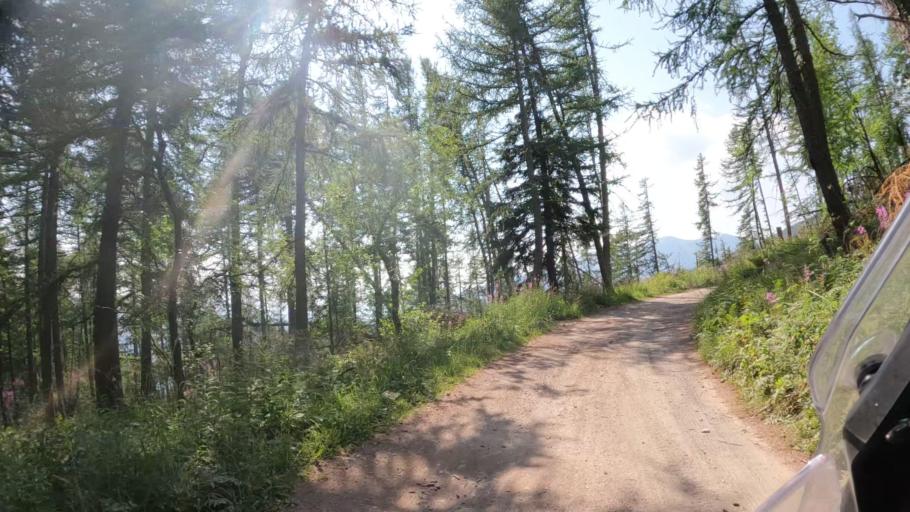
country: IT
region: Piedmont
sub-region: Provincia di Cuneo
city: Briga Alta
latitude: 44.0960
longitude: 7.7226
